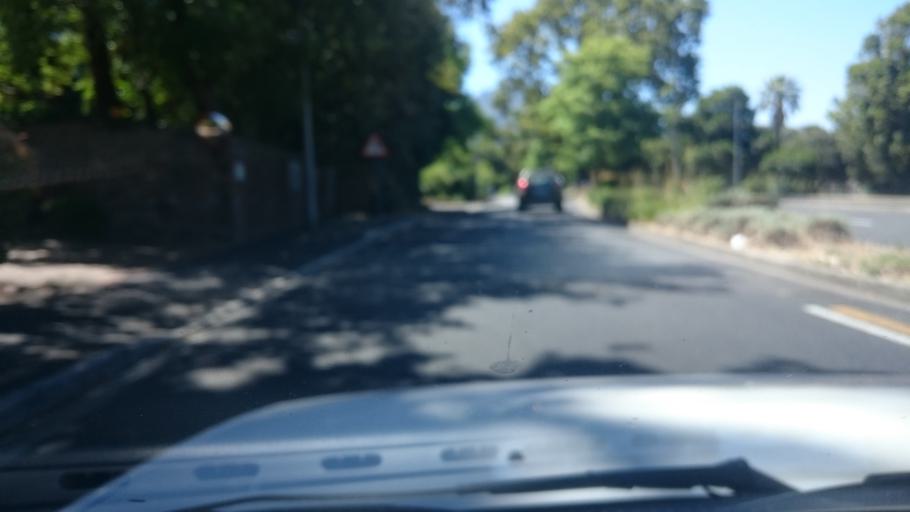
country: ZA
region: Western Cape
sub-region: City of Cape Town
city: Claremont
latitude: -34.0034
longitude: 18.4613
